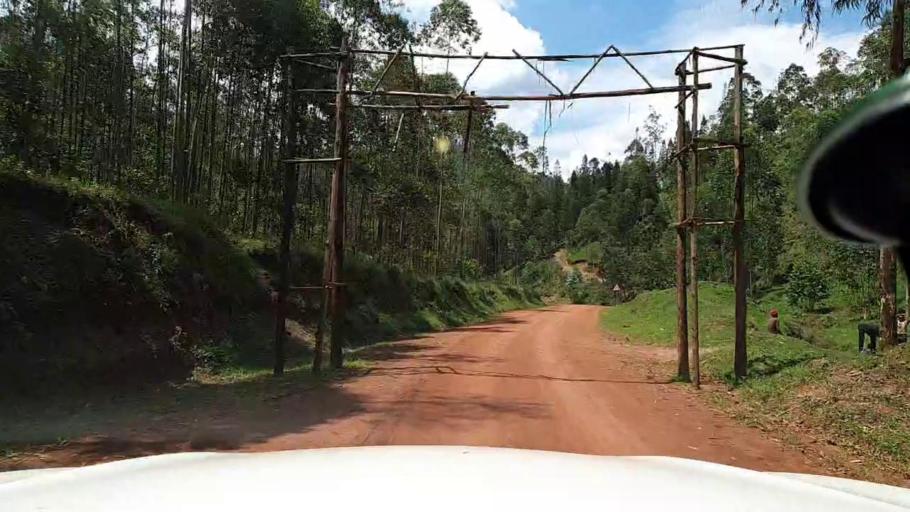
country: RW
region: Northern Province
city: Byumba
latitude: -1.7002
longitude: 29.8341
